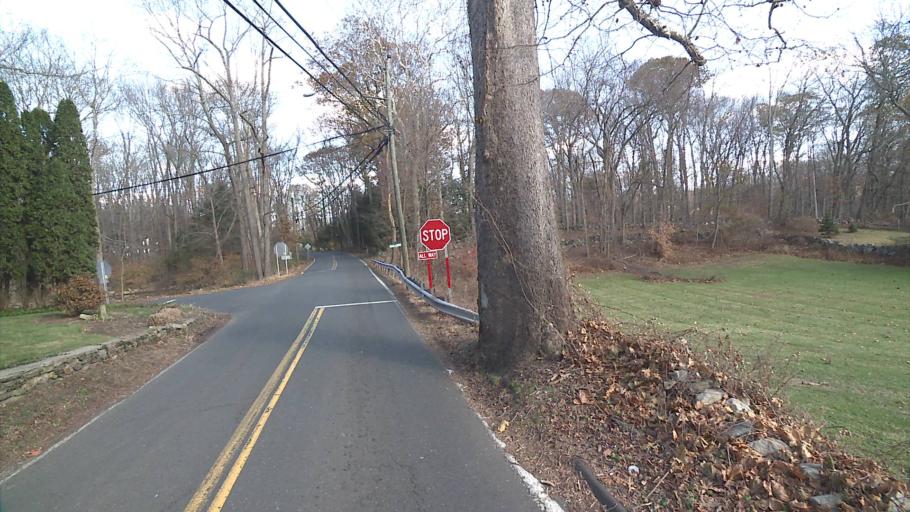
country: US
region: Connecticut
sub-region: Fairfield County
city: Wilton
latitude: 41.1975
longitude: -73.3947
